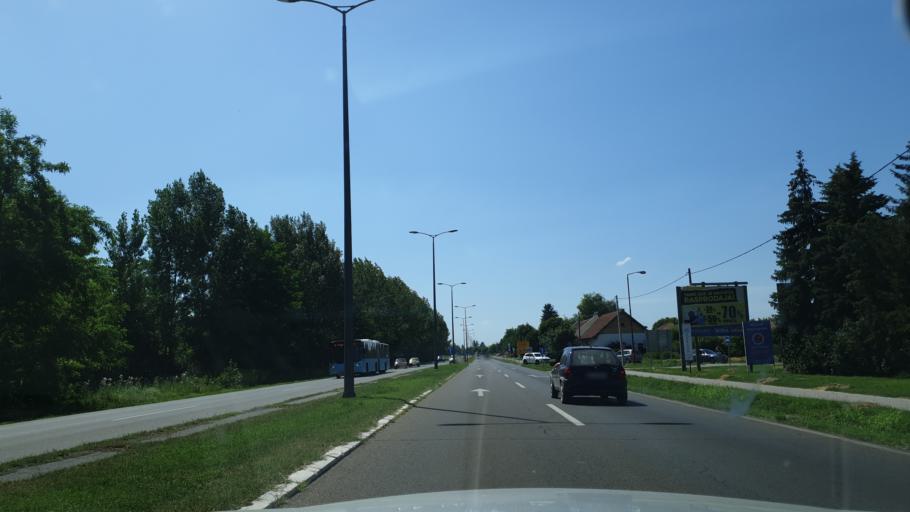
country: RS
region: Autonomna Pokrajina Vojvodina
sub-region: Severnobacki Okrug
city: Subotica
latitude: 46.1043
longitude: 19.7366
